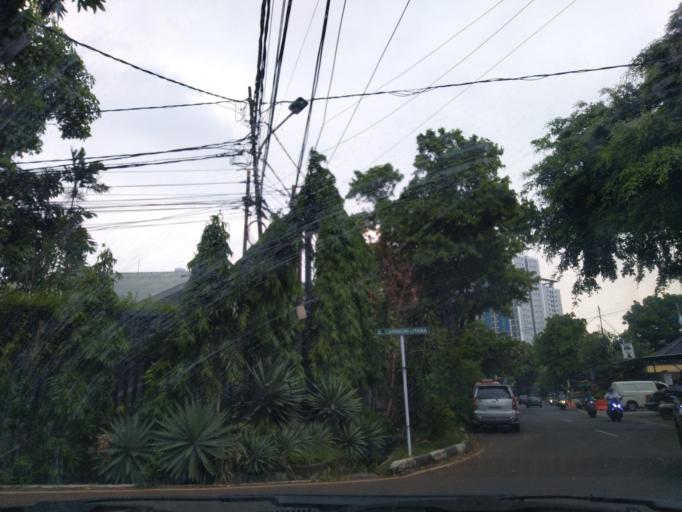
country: ID
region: Banten
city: South Tangerang
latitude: -6.2835
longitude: 106.7935
